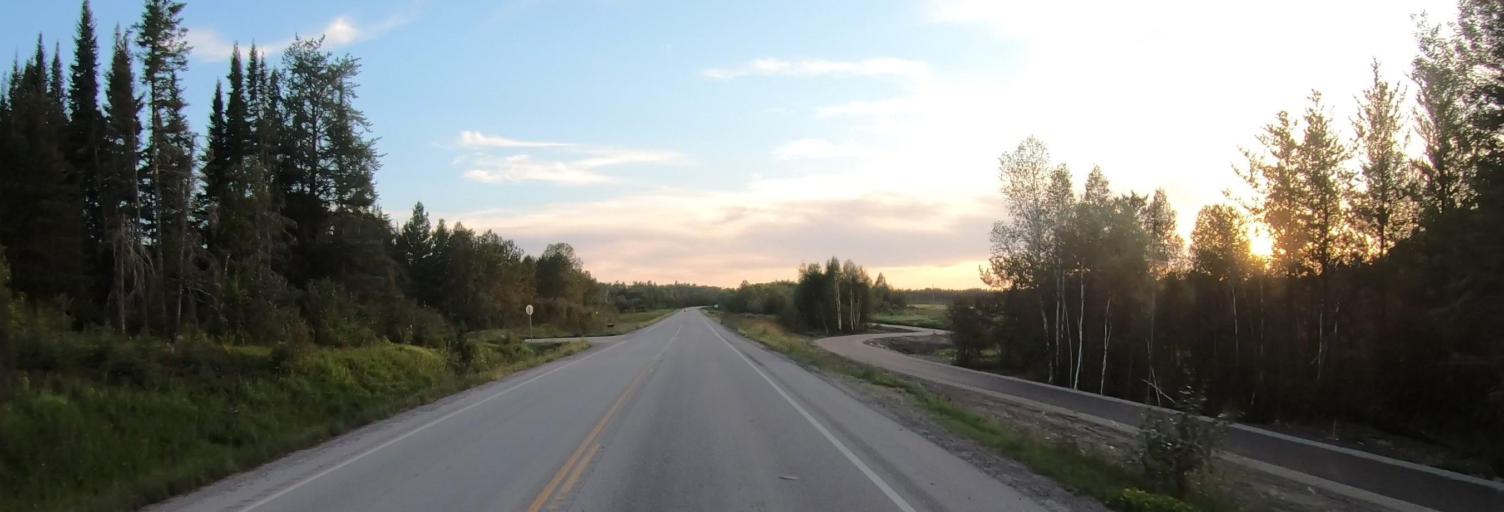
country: US
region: Minnesota
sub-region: Saint Louis County
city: Ely
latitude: 47.8849
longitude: -91.9538
